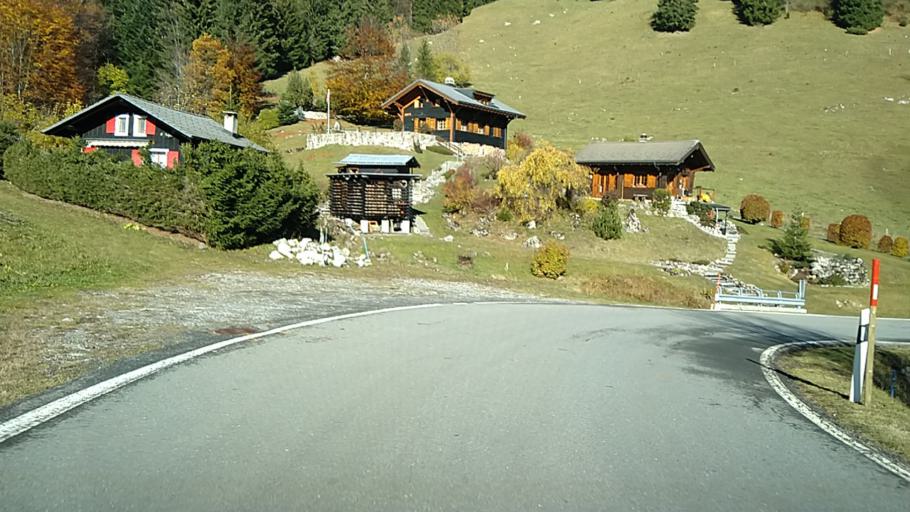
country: CH
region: Valais
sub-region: Monthey District
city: Tanay
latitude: 46.3145
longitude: 6.8505
